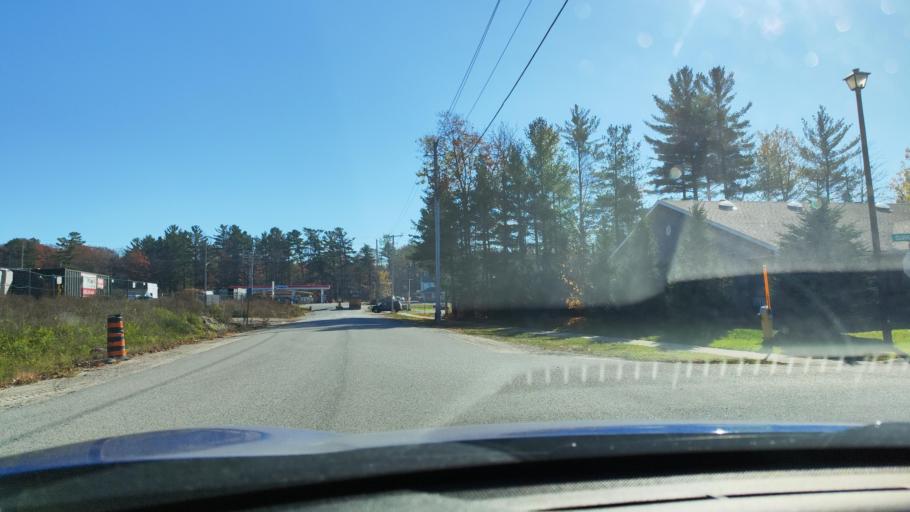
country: CA
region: Ontario
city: Wasaga Beach
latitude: 44.5280
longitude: -79.9975
